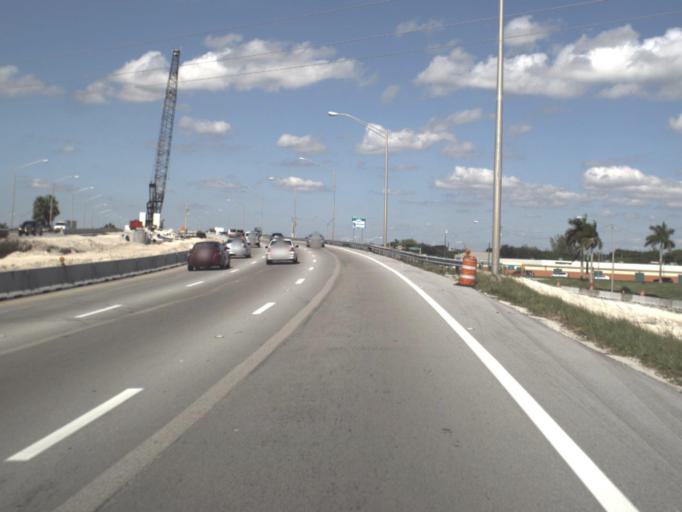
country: US
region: Florida
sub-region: Miami-Dade County
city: South Miami Heights
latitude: 25.5936
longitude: -80.3701
